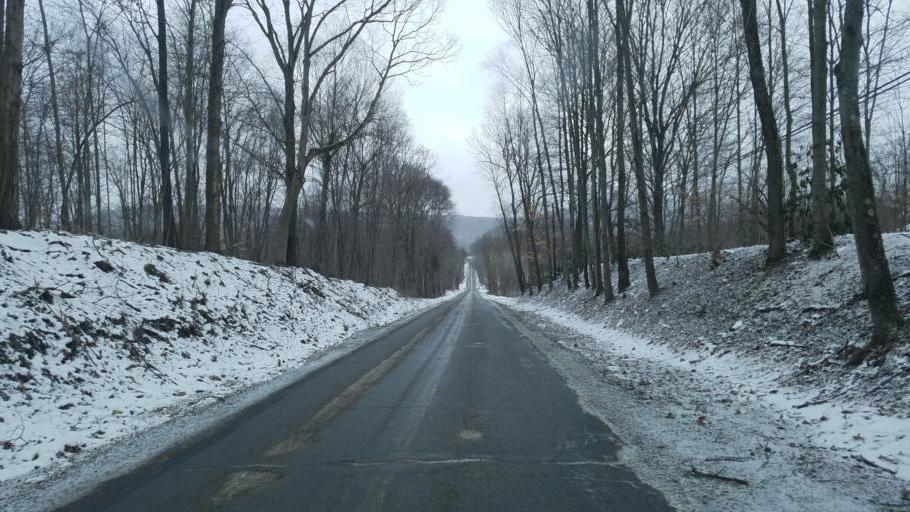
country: US
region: Pennsylvania
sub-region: Crawford County
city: Cochranton
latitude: 41.4775
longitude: -80.0061
